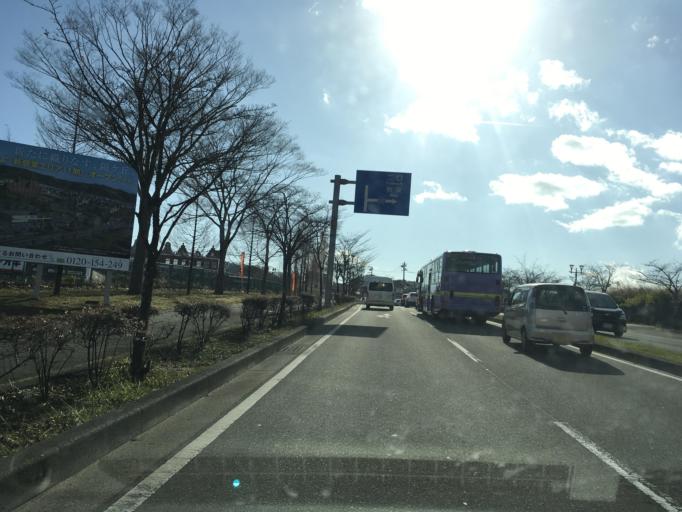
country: JP
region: Miyagi
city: Sendai
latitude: 38.2602
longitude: 140.7631
